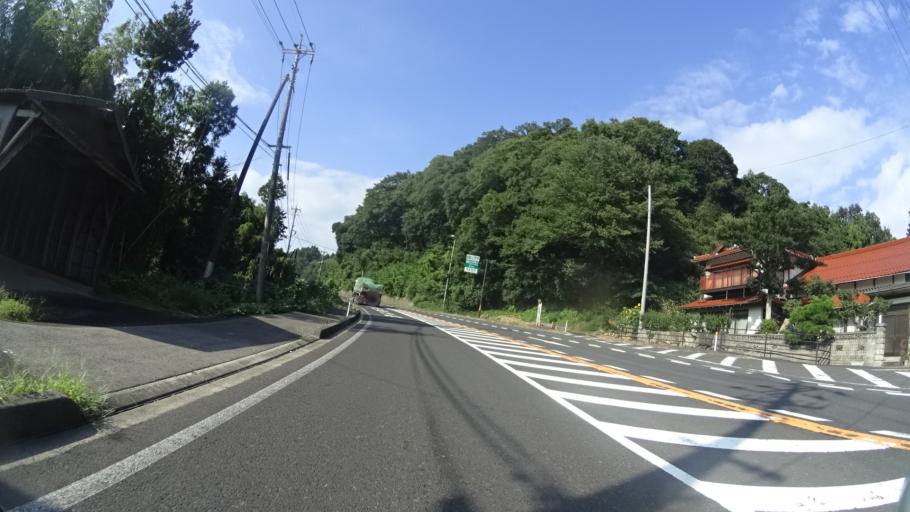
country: JP
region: Shimane
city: Odacho-oda
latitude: 35.2611
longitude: 132.5780
